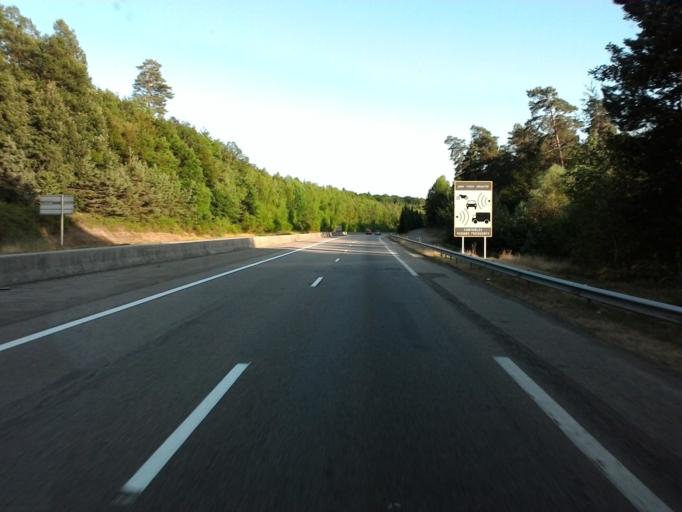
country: FR
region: Lorraine
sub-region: Departement des Vosges
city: Epinal
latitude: 48.1669
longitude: 6.4859
